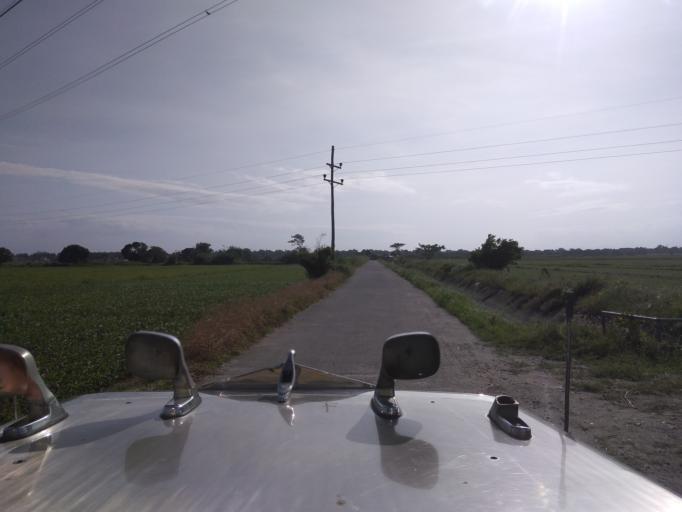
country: PH
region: Central Luzon
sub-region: Province of Pampanga
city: San Patricio
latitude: 15.1021
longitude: 120.7021
